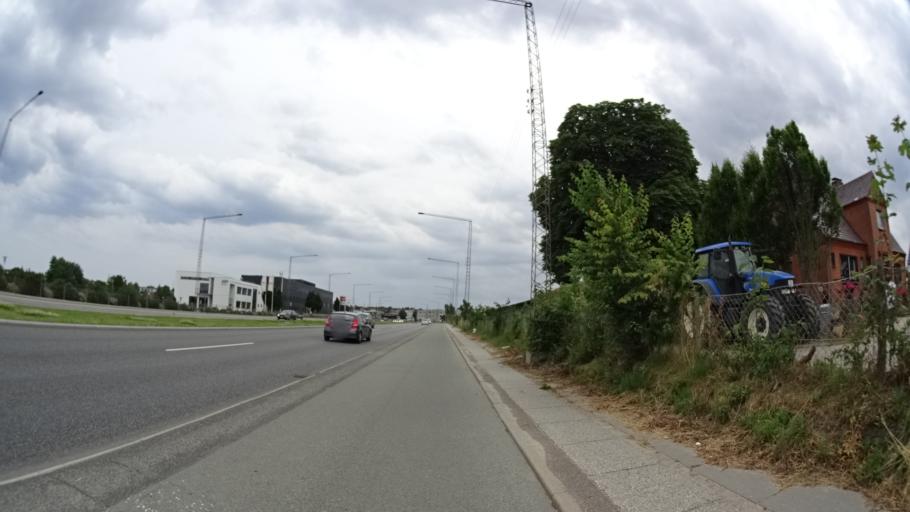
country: DK
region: Central Jutland
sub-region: Arhus Kommune
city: Stavtrup
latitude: 56.1339
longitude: 10.1566
